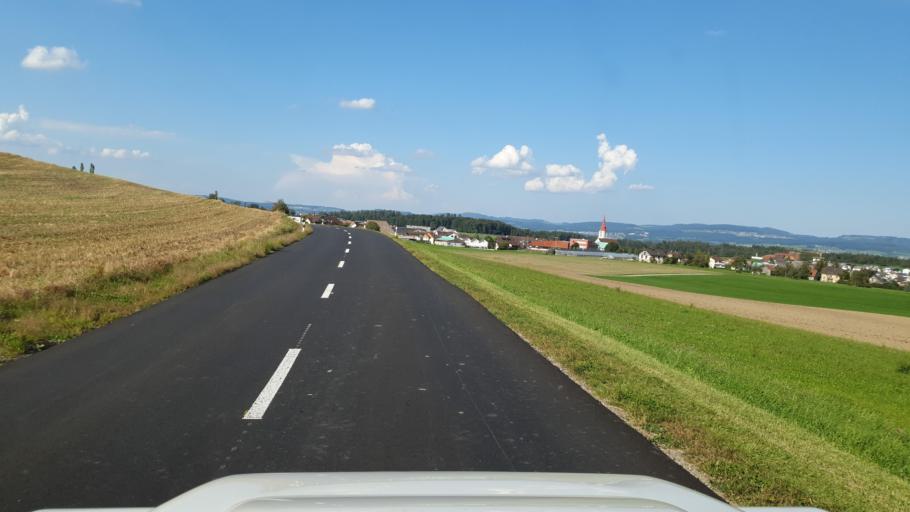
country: CH
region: Aargau
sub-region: Bezirk Muri
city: Auw
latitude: 47.2053
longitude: 8.3608
